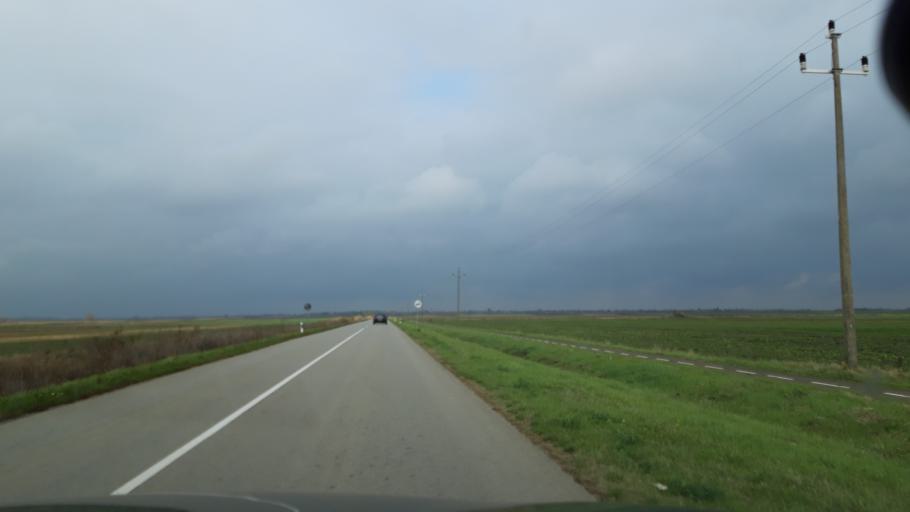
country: HU
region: Csongrad
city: Roszke
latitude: 46.1347
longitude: 20.0933
